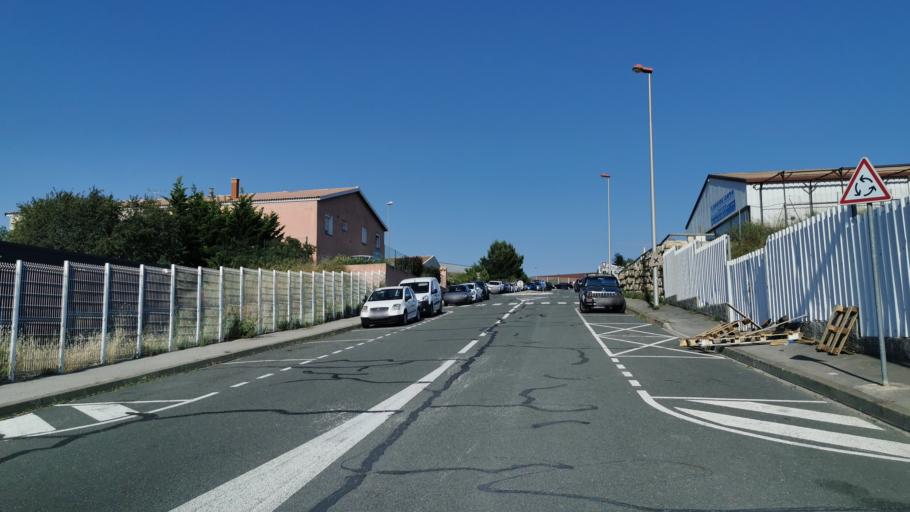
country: FR
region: Languedoc-Roussillon
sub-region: Departement de l'Aude
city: Narbonne
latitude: 43.1589
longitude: 2.9838
